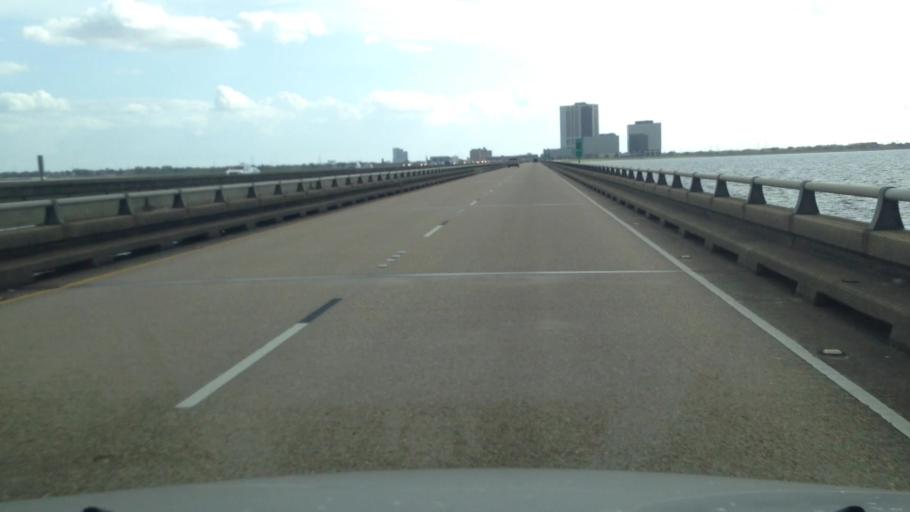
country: US
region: Louisiana
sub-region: Jefferson Parish
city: Metairie
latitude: 30.0368
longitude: -90.1515
